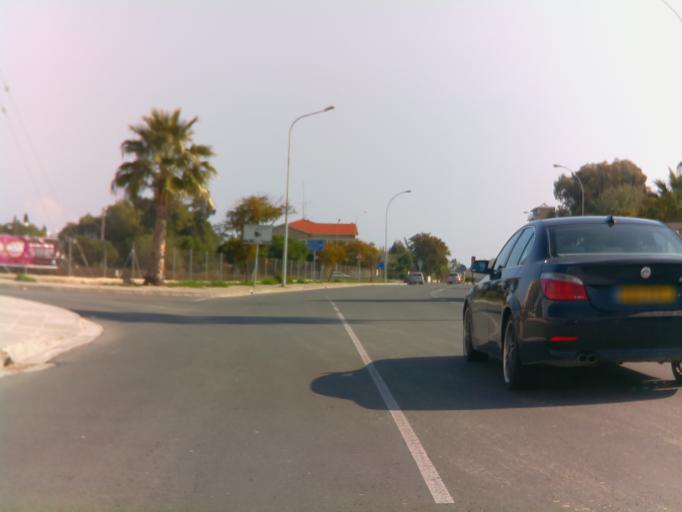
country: CY
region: Larnaka
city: Larnaca
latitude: 34.9113
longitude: 33.6269
